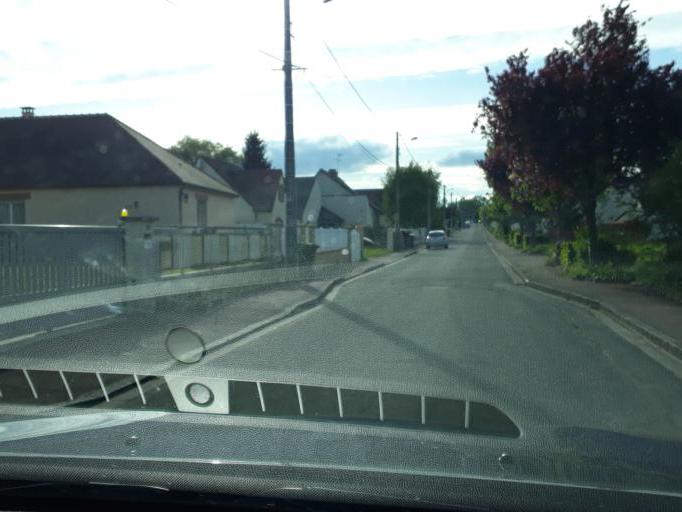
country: FR
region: Centre
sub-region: Departement du Loiret
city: Saint-Jean-de-la-Ruelle
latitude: 47.9222
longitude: 1.8702
